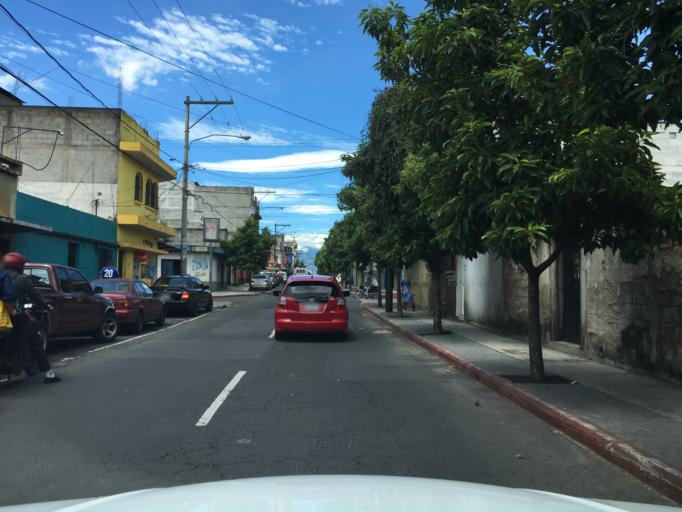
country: GT
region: Guatemala
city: Guatemala City
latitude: 14.6225
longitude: -90.5410
